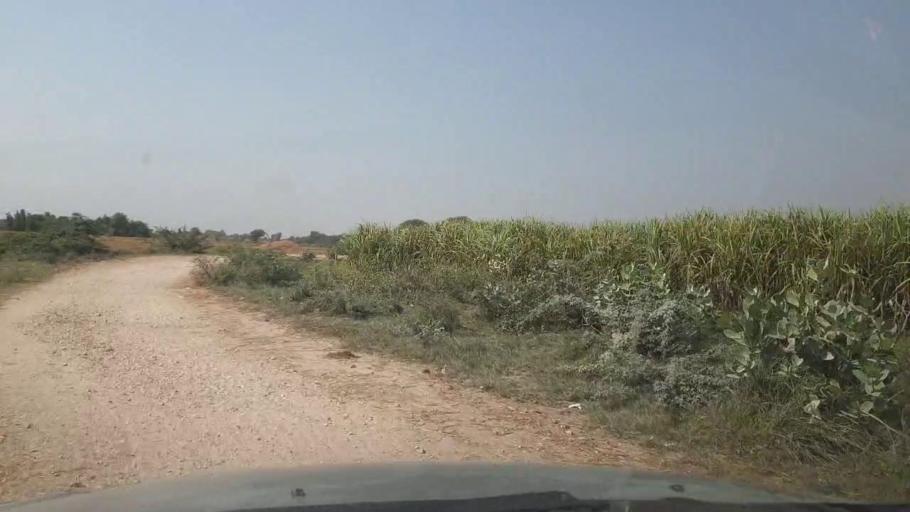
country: PK
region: Sindh
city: Bulri
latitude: 24.8698
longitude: 68.3222
